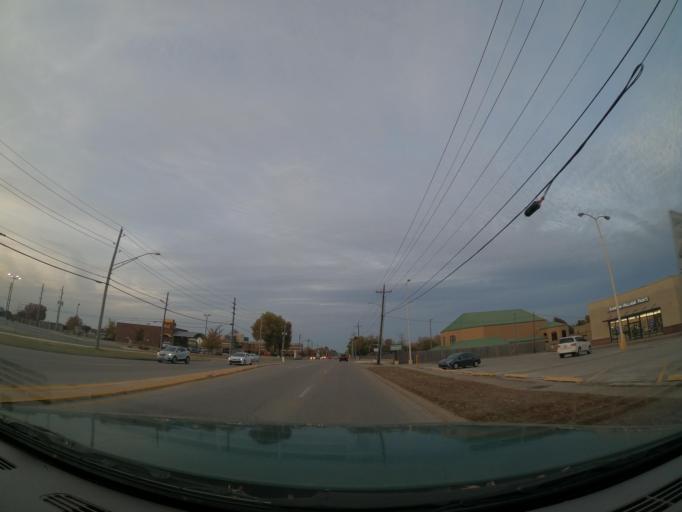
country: US
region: Oklahoma
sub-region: Tulsa County
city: Broken Arrow
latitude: 36.0188
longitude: -95.7974
